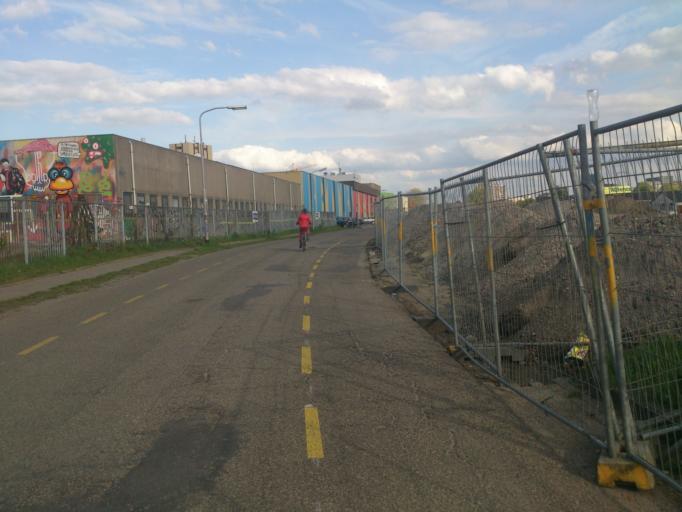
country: NL
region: Gelderland
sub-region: Gemeente Nijmegen
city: Nijmegen
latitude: 51.8544
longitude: 5.8426
